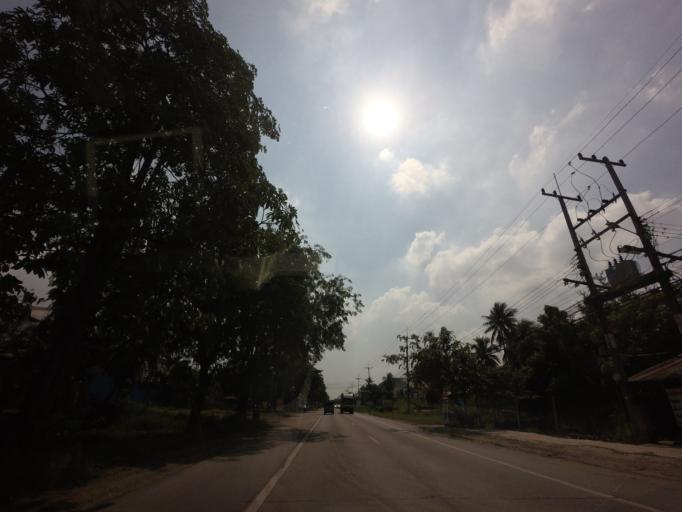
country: TH
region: Nakhon Pathom
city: Sam Phran
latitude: 13.7616
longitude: 100.2310
